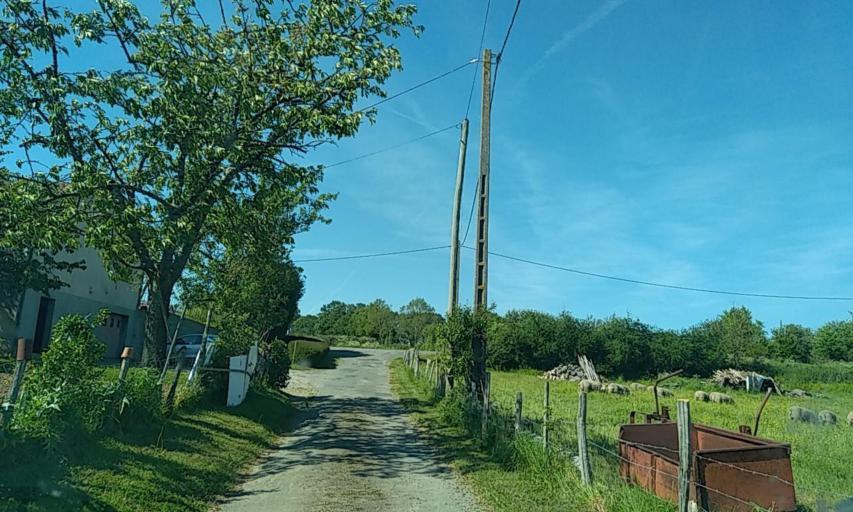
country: FR
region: Poitou-Charentes
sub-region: Departement des Deux-Sevres
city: Boisme
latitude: 46.7761
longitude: -0.4257
